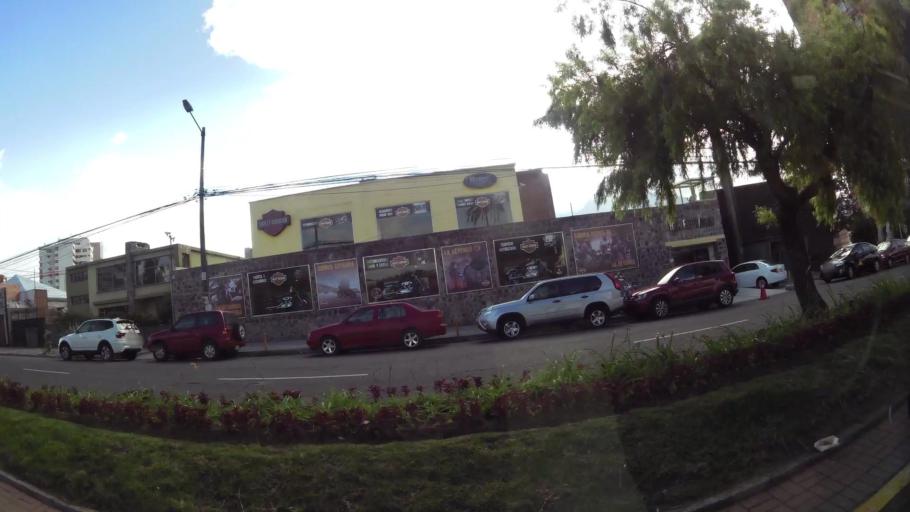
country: EC
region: Pichincha
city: Quito
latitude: -0.2011
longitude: -78.4802
